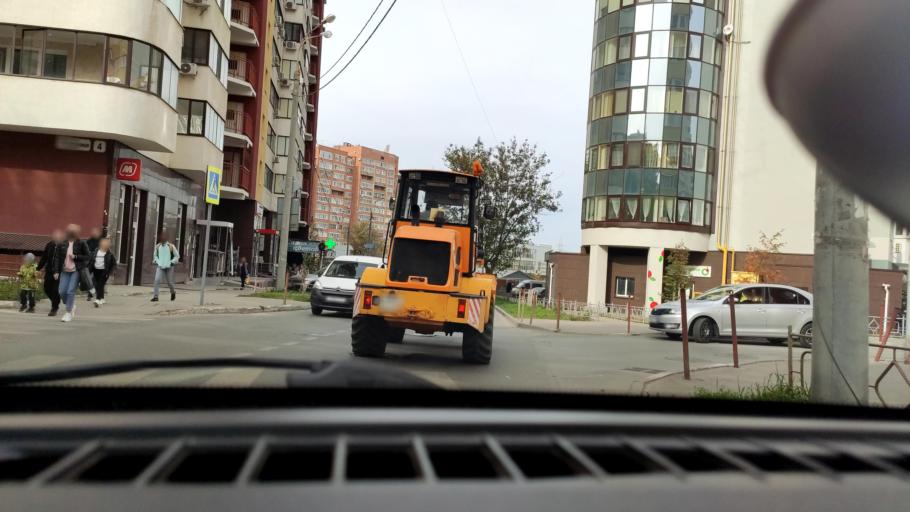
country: RU
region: Samara
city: Samara
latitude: 53.2172
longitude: 50.1657
